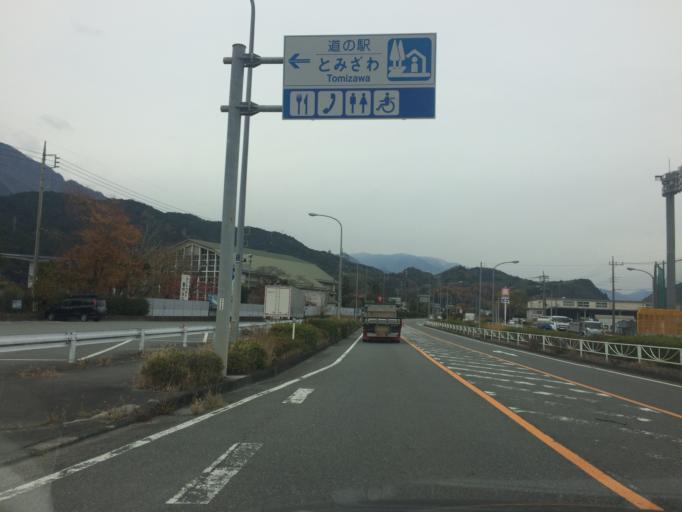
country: JP
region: Shizuoka
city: Fujinomiya
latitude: 35.2420
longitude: 138.4852
